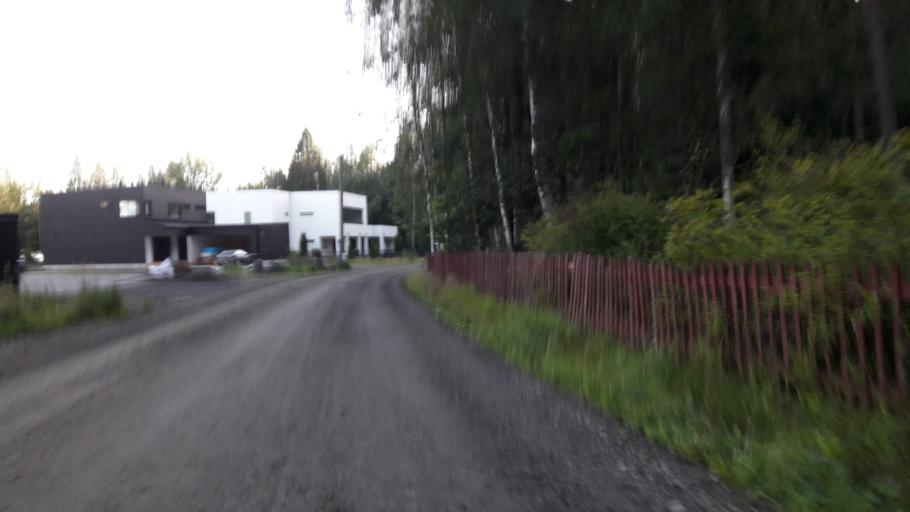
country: FI
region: North Karelia
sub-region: Joensuu
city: Joensuu
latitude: 62.6149
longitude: 29.6990
